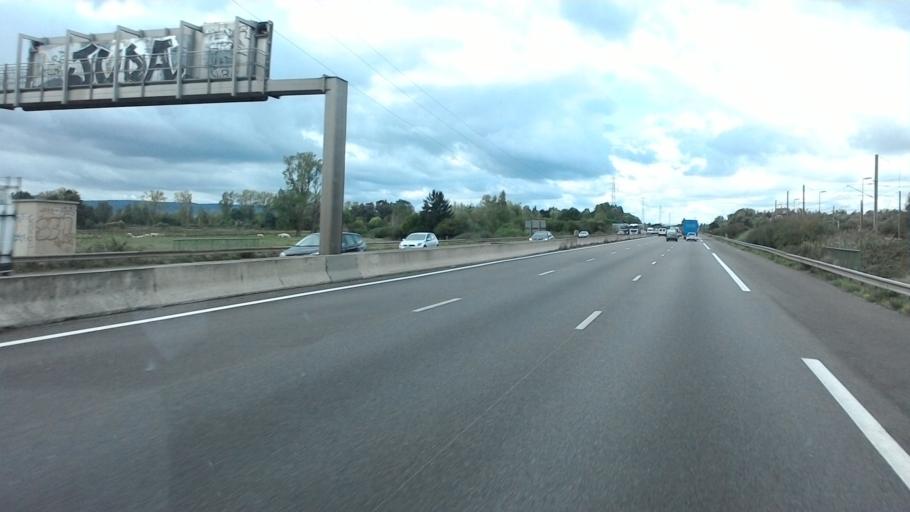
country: FR
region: Lorraine
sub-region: Departement de la Moselle
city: Argancy
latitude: 49.1707
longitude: 6.1803
